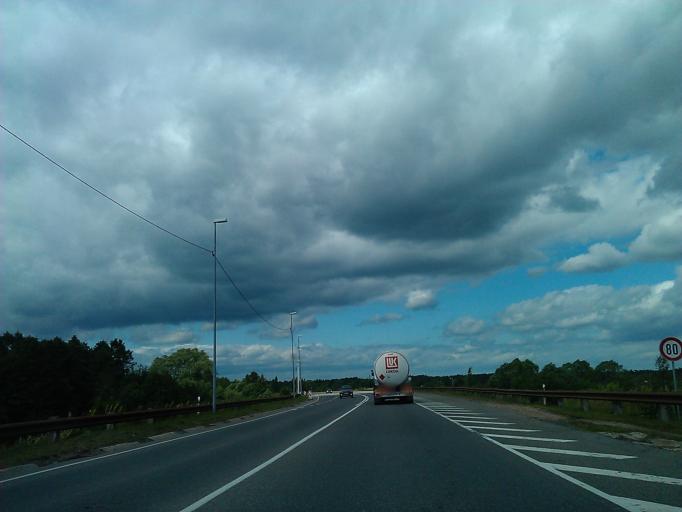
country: LV
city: Tireli
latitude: 56.9313
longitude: 23.6082
